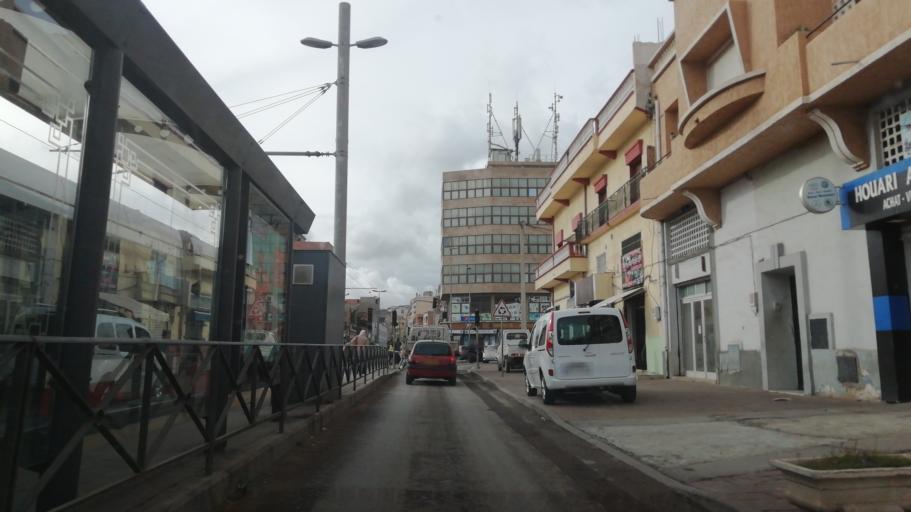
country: DZ
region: Oran
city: Oran
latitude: 35.6981
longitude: -0.6179
